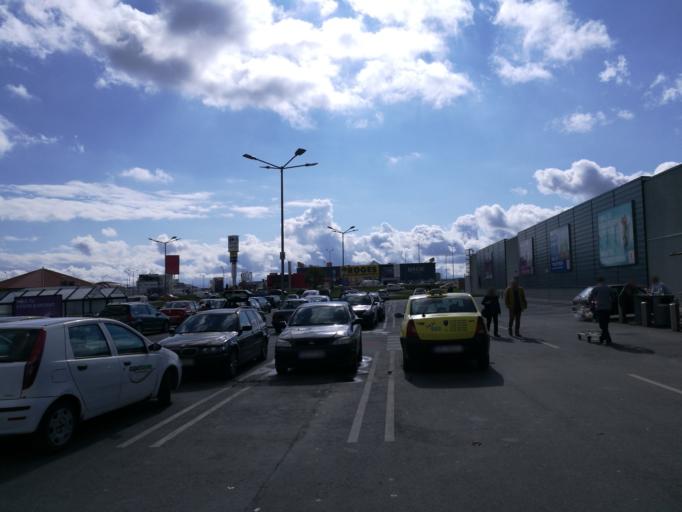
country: RO
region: Sibiu
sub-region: Municipiul Sibiu
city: Sibiu
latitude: 45.7800
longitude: 24.1674
